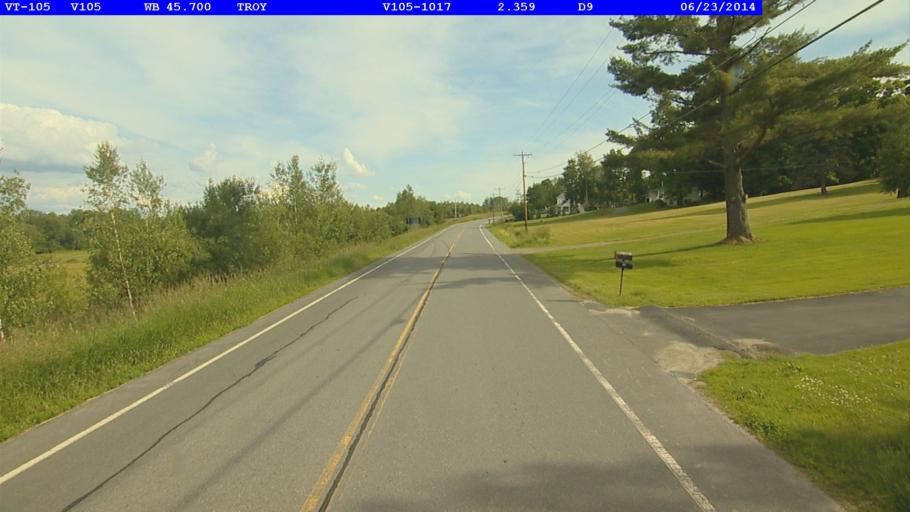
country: US
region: Vermont
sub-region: Orleans County
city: Newport
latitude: 44.9922
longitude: -72.4078
